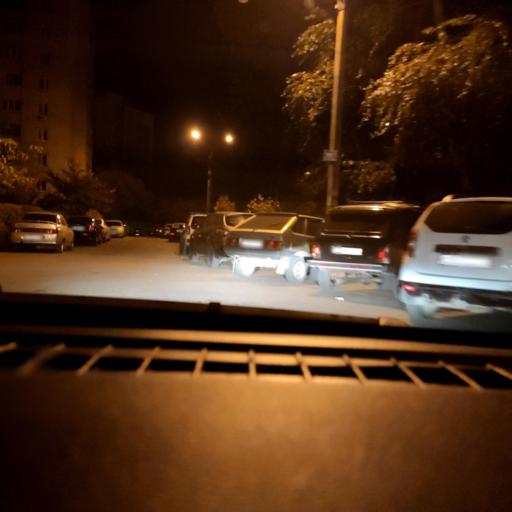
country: RU
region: Voronezj
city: Voronezh
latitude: 51.6420
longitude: 39.1446
